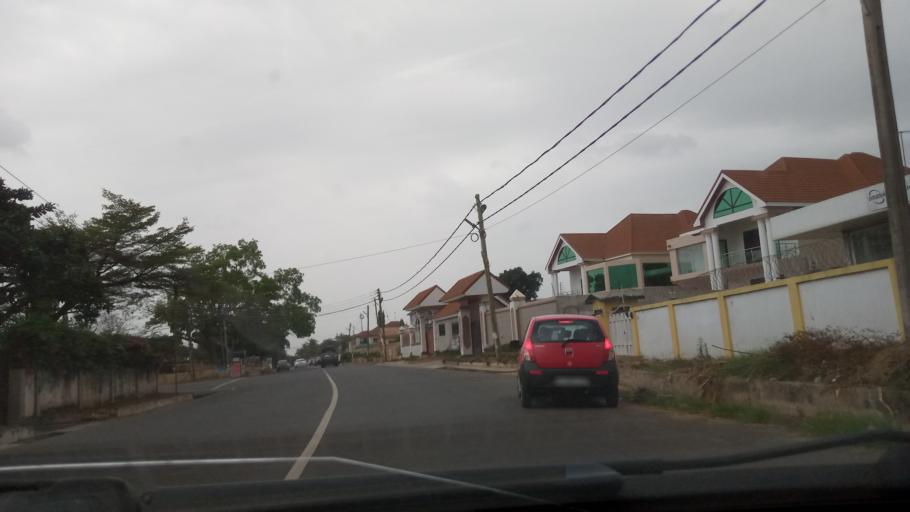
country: GH
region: Greater Accra
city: Dome
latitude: 5.6152
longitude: -0.2032
